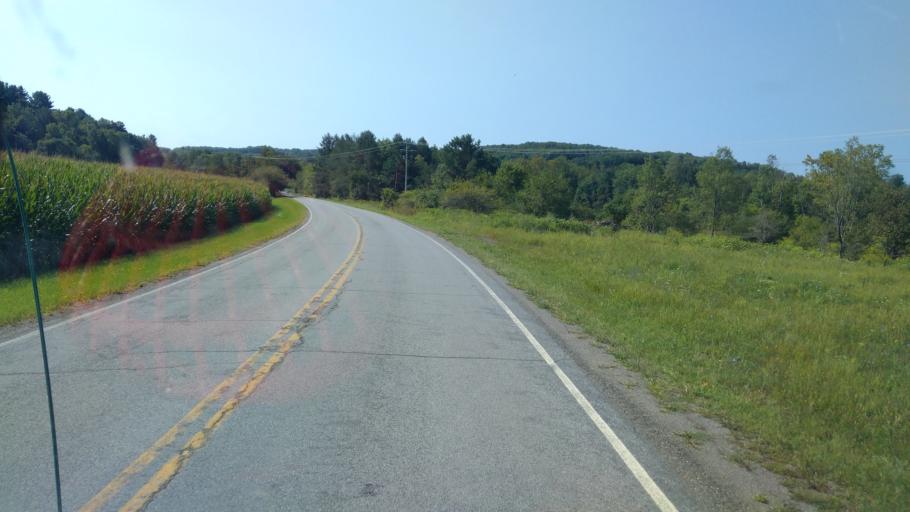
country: US
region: New York
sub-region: Allegany County
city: Friendship
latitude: 42.1753
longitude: -78.1487
